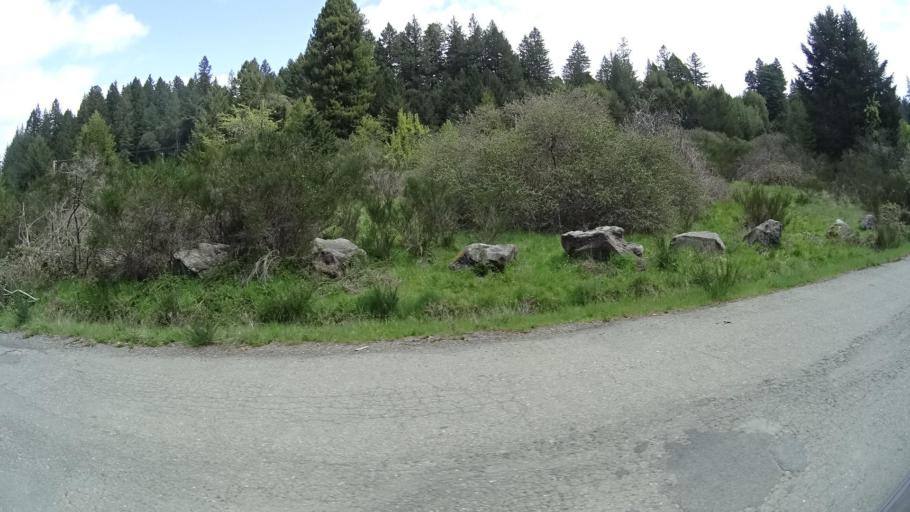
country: US
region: California
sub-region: Humboldt County
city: Redway
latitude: 40.0176
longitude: -123.9367
